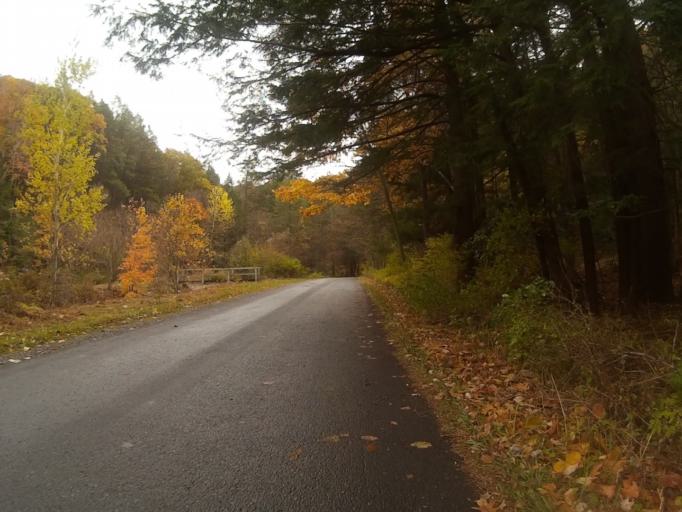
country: US
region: Pennsylvania
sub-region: Centre County
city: Boalsburg
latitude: 40.7646
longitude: -77.7560
